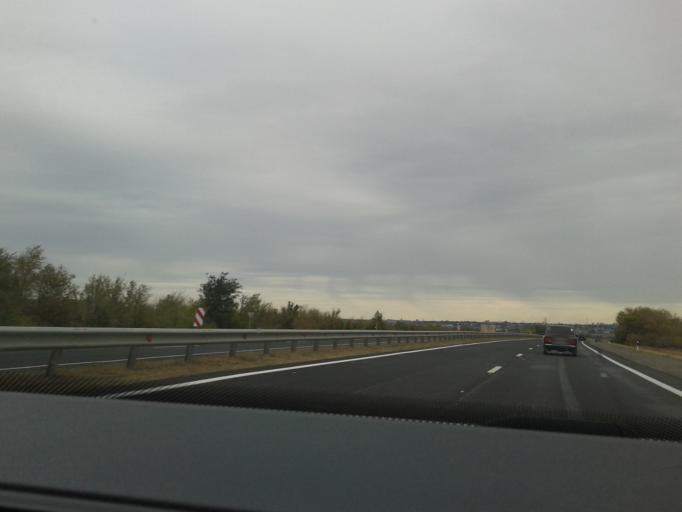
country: RU
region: Volgograd
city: Gorodishche
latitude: 48.8222
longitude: 44.4362
